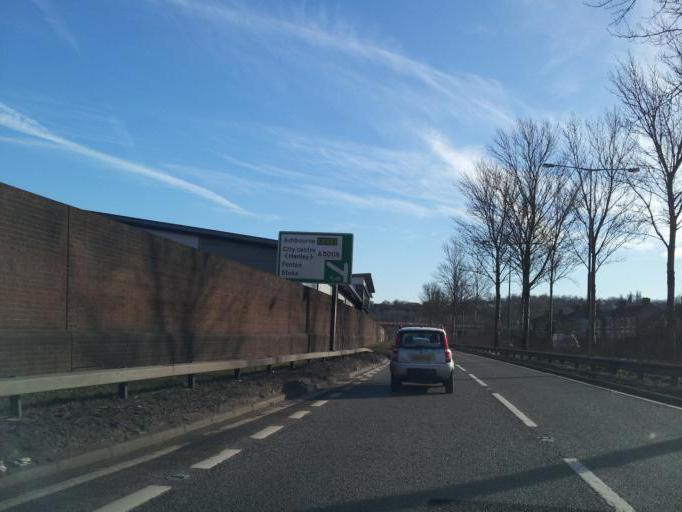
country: GB
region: England
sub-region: Stoke-on-Trent
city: Stoke-on-Trent
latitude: 53.0154
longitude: -2.2012
